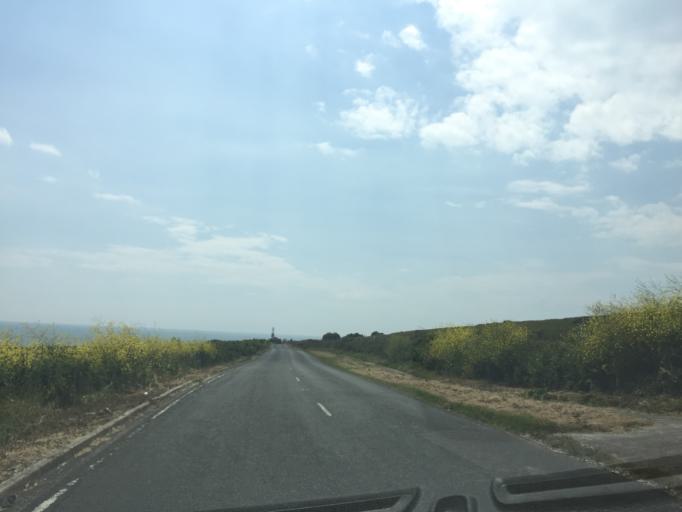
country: GB
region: England
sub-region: Dorset
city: Easton
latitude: 50.5252
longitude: -2.4426
